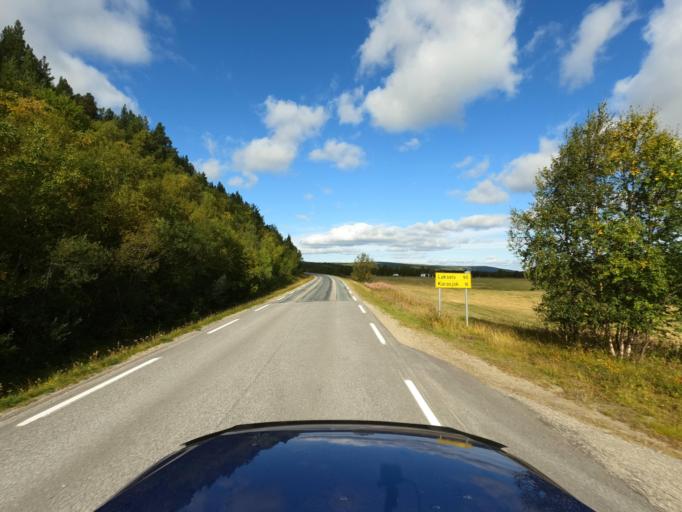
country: NO
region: Finnmark Fylke
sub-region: Karasjok
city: Karasjohka
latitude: 69.4108
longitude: 25.8050
